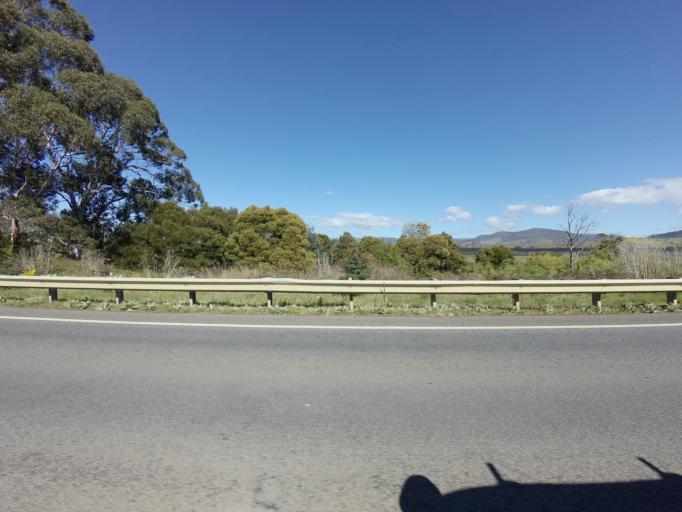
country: AU
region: Tasmania
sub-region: Derwent Valley
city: New Norfolk
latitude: -42.7337
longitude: 146.9662
